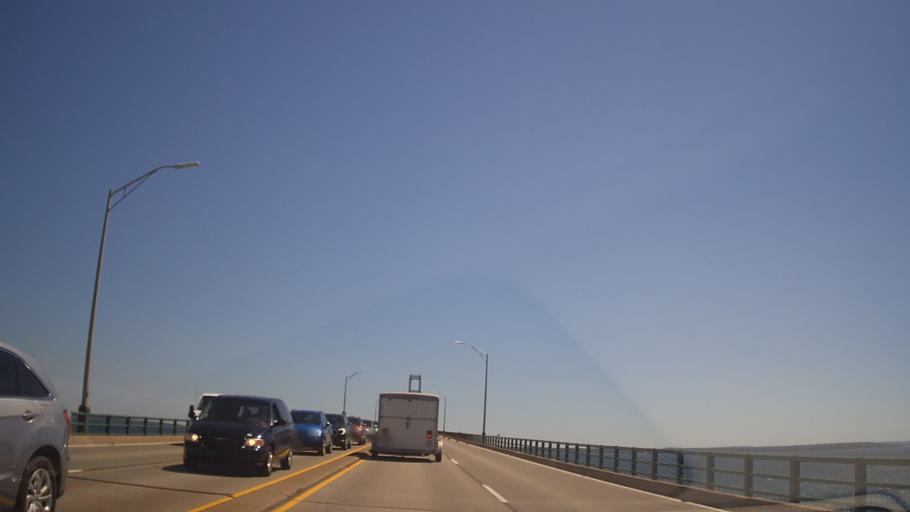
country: US
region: Michigan
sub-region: Mackinac County
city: Saint Ignace
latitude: 45.8360
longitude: -84.7250
